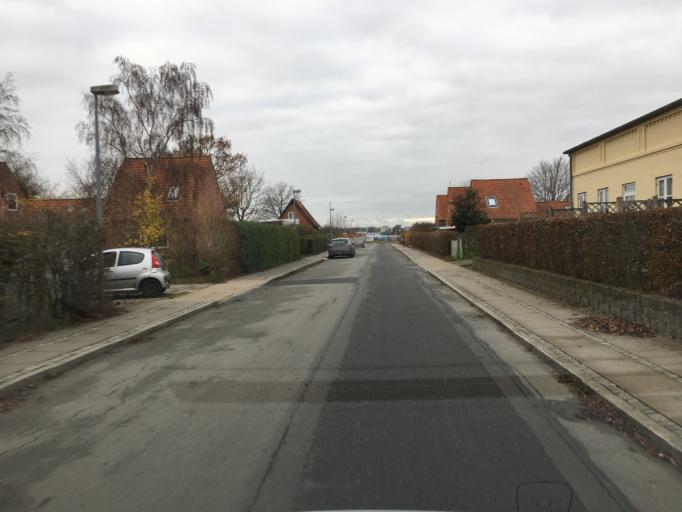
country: DK
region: South Denmark
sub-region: Tonder Kommune
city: Tonder
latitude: 54.9458
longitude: 8.8680
